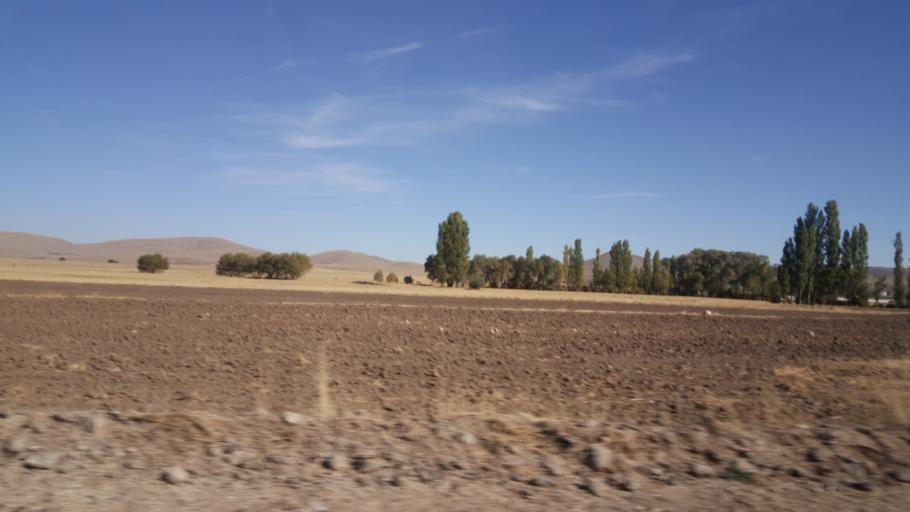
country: TR
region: Ankara
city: Altpinar
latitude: 39.2730
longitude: 32.7547
